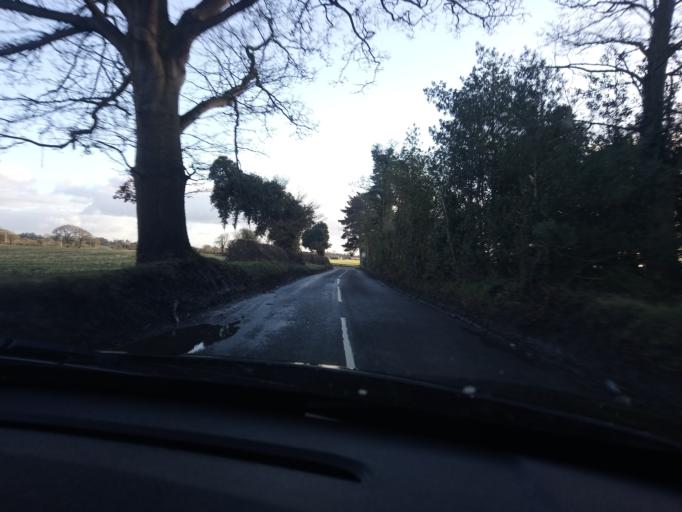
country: GB
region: England
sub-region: Shropshire
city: Petton
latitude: 52.8837
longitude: -2.7866
